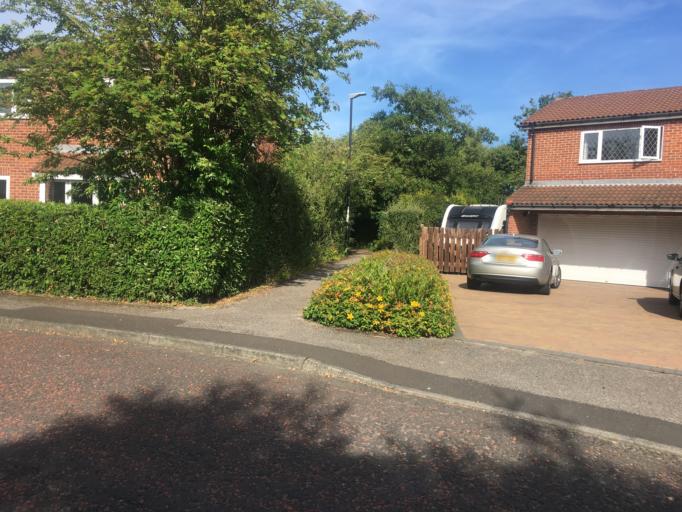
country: GB
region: England
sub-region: County Durham
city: Chester-le-Street
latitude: 54.8763
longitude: -1.5543
